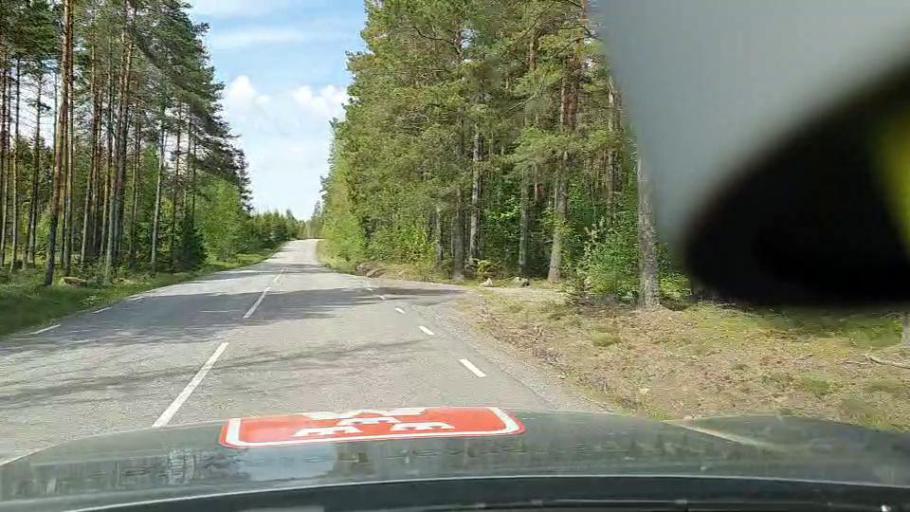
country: SE
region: Soedermanland
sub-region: Eskilstuna Kommun
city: Skogstorp
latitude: 59.2669
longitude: 16.4701
